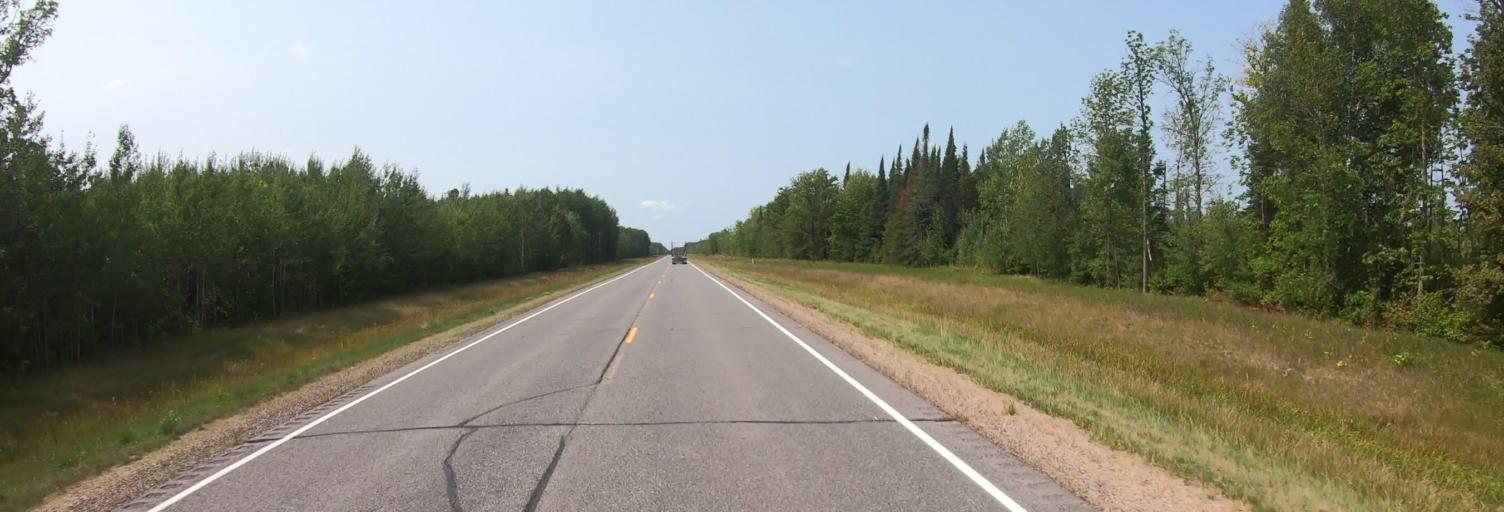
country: US
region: Minnesota
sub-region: Koochiching County
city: International Falls
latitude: 48.5126
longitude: -93.7457
